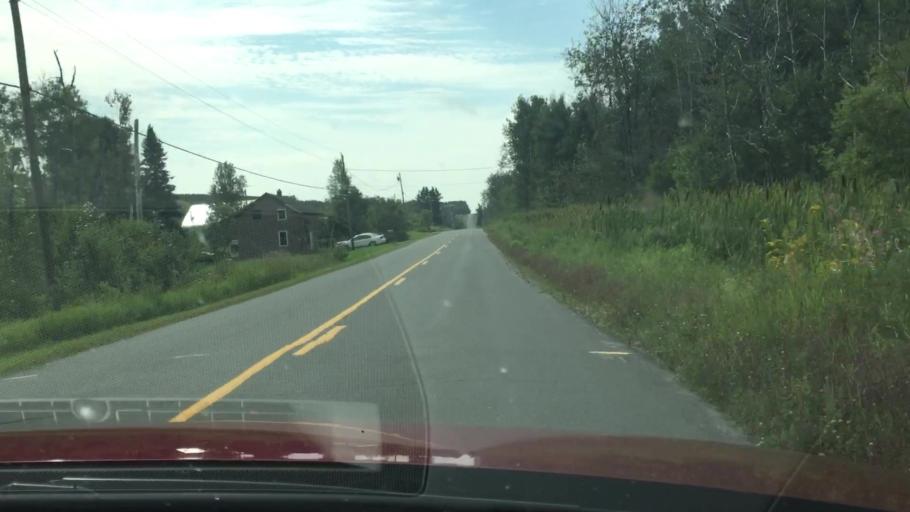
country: US
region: Maine
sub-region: Aroostook County
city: Caribou
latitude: 46.8147
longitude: -68.0246
